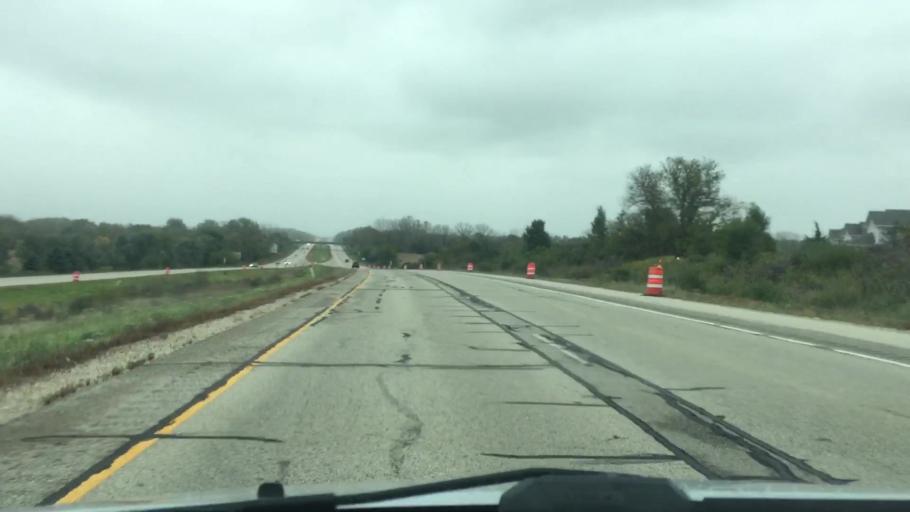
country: US
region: Wisconsin
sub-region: Walworth County
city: Lake Geneva
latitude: 42.5856
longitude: -88.4006
